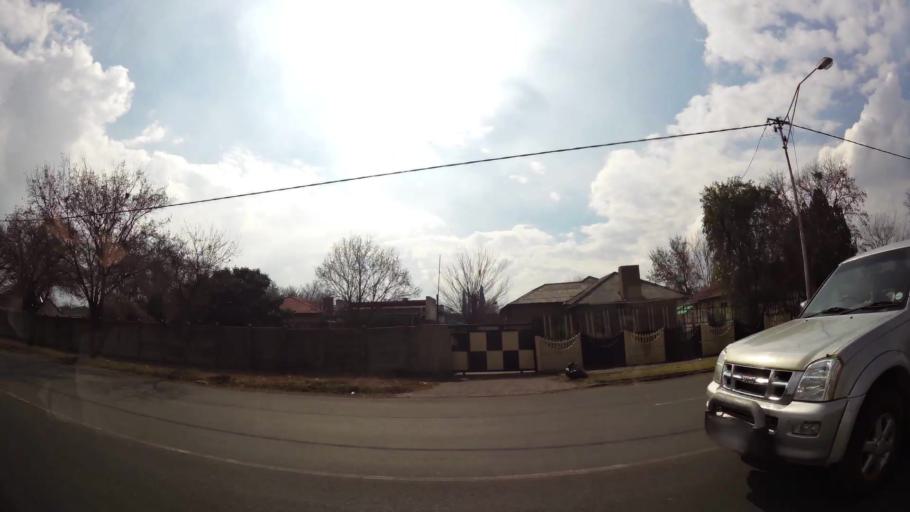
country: ZA
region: Gauteng
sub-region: Sedibeng District Municipality
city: Vereeniging
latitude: -26.6826
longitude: 27.9192
